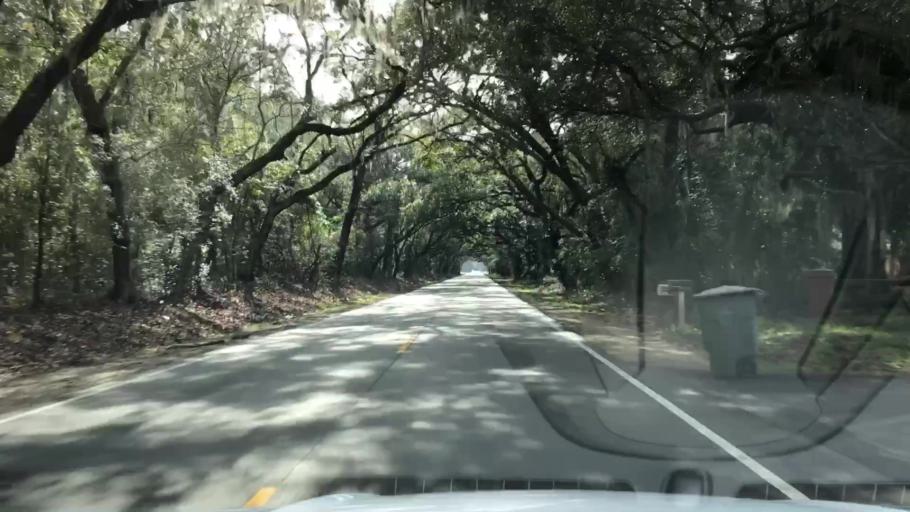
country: US
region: South Carolina
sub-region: Charleston County
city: Folly Beach
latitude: 32.7097
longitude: -80.0177
